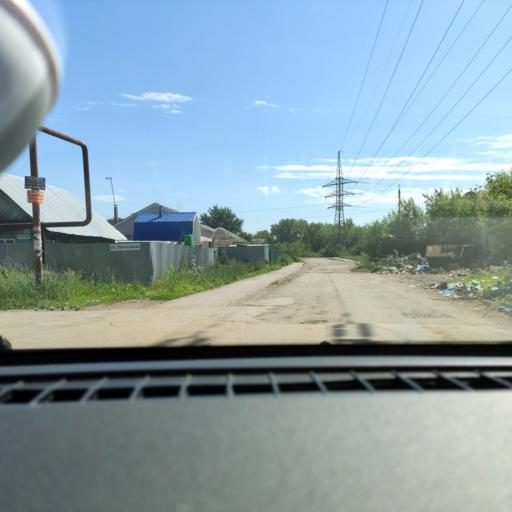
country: RU
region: Samara
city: Samara
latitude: 53.1330
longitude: 50.1245
